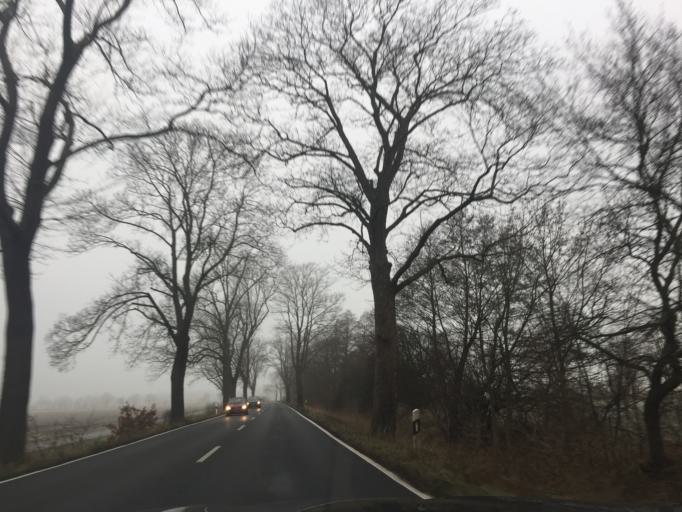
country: DE
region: Brandenburg
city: Velten
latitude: 52.6606
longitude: 13.1755
